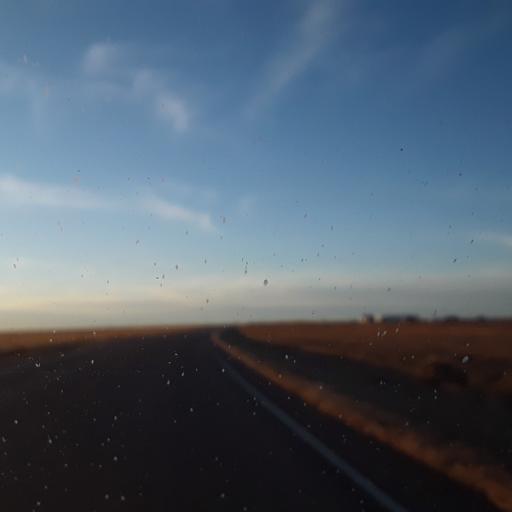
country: US
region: Colorado
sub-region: Cheyenne County
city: Cheyenne Wells
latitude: 38.8092
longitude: -102.4536
